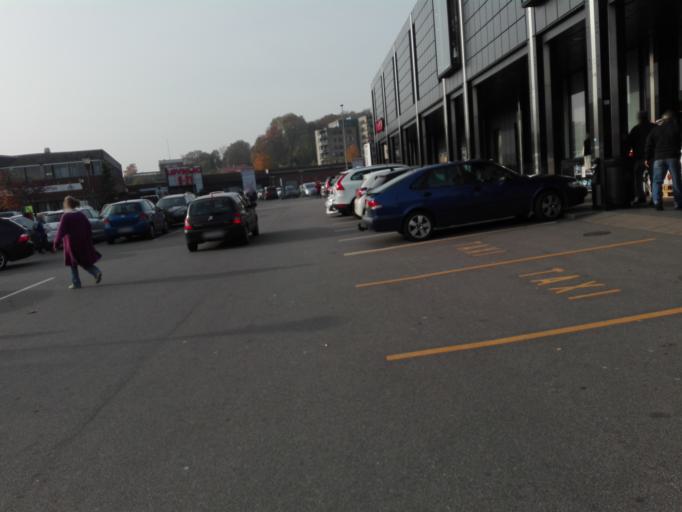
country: DK
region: Central Jutland
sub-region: Odder Kommune
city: Odder
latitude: 55.9760
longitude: 10.1502
